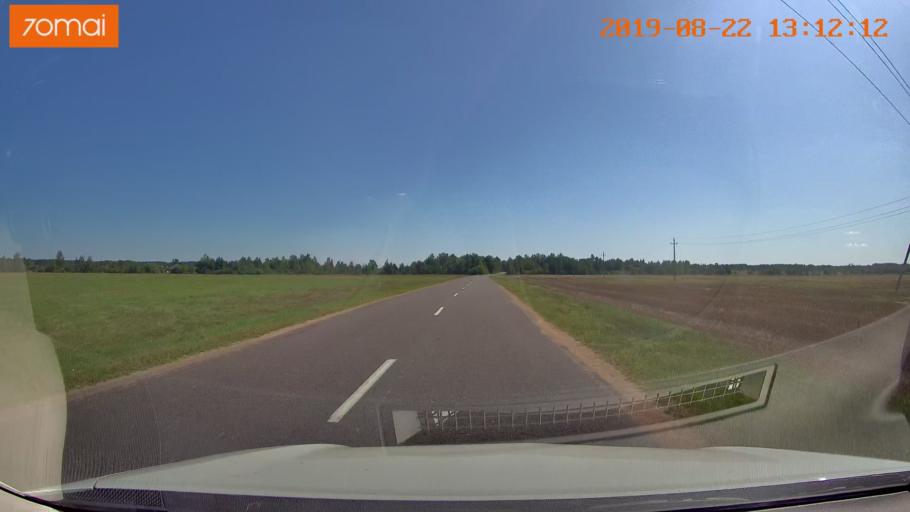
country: BY
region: Minsk
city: Prawdzinski
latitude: 53.2717
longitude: 27.8594
